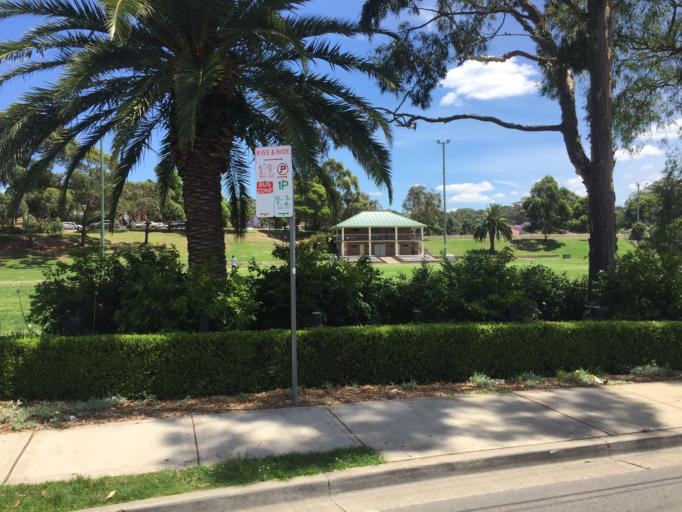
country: AU
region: New South Wales
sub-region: Ryde
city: Denistone
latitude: -33.7896
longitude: 151.0817
